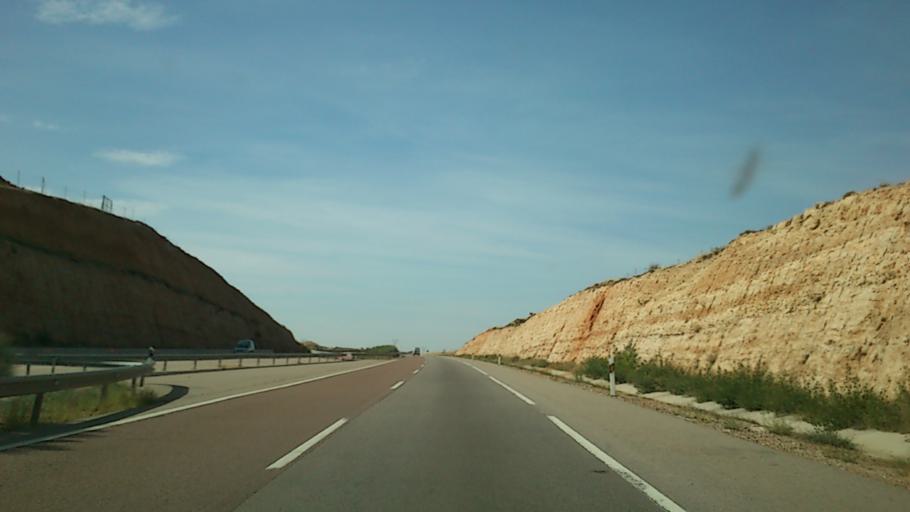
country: ES
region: Aragon
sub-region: Provincia de Teruel
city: Ferreruela de Huerva
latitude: 40.9961
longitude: -1.2616
